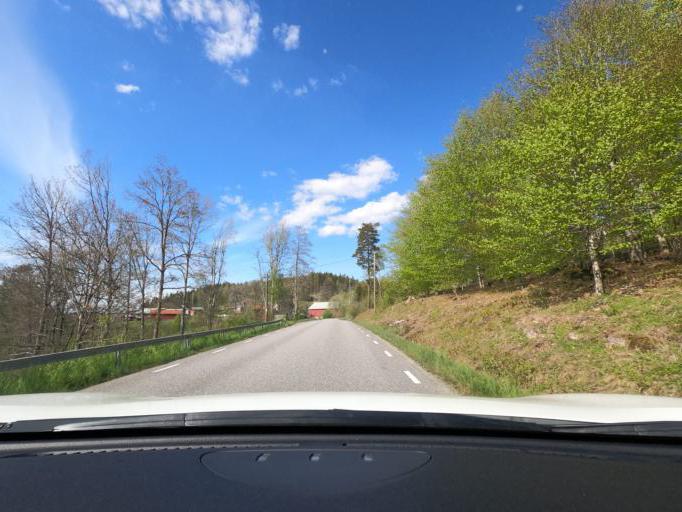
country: SE
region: Vaestra Goetaland
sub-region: Harryda Kommun
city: Ravlanda
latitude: 57.6333
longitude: 12.4983
